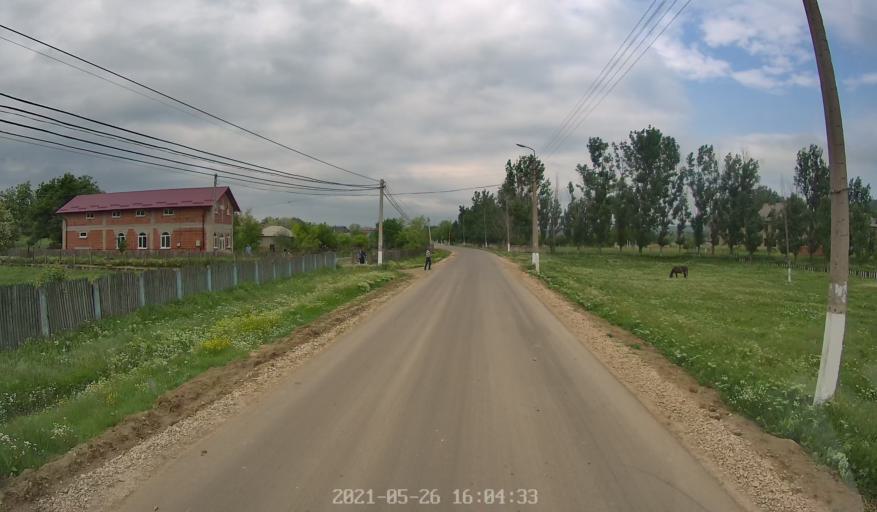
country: RO
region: Vaslui
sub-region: Comuna Stanilesti
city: Stanilesti
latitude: 46.6524
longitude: 28.3043
